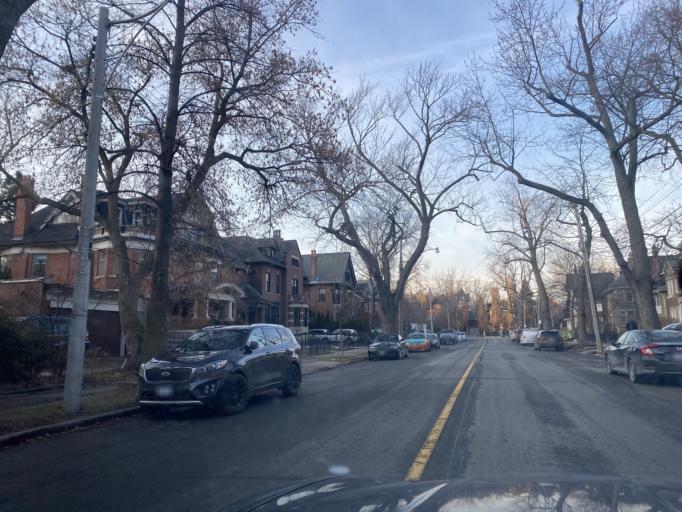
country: CA
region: Ontario
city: Toronto
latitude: 43.6754
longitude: -79.3780
